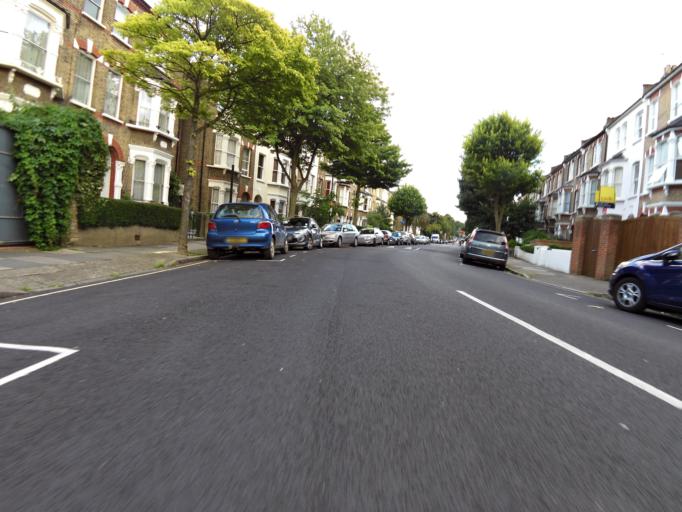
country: GB
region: England
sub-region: Greater London
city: Holloway
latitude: 51.5590
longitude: -0.1308
